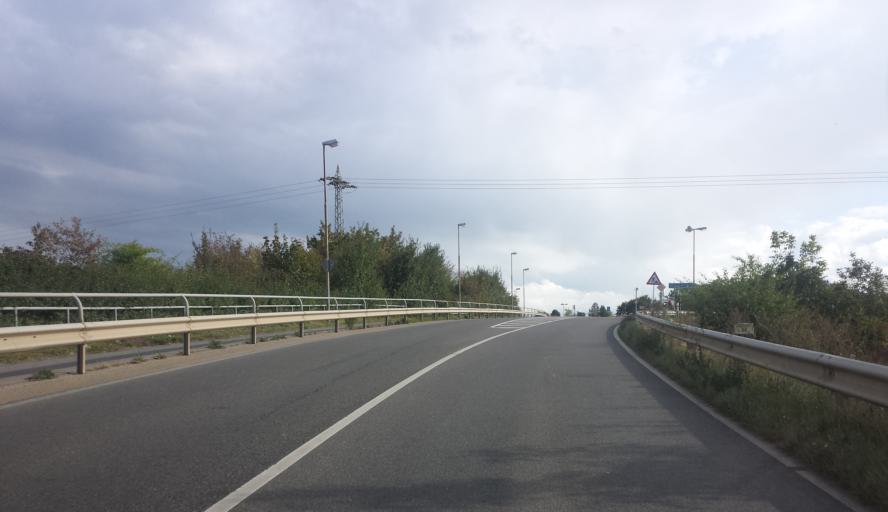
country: DE
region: Rheinland-Pfalz
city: Dannstadt-Schauernheim
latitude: 49.4355
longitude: 8.3056
